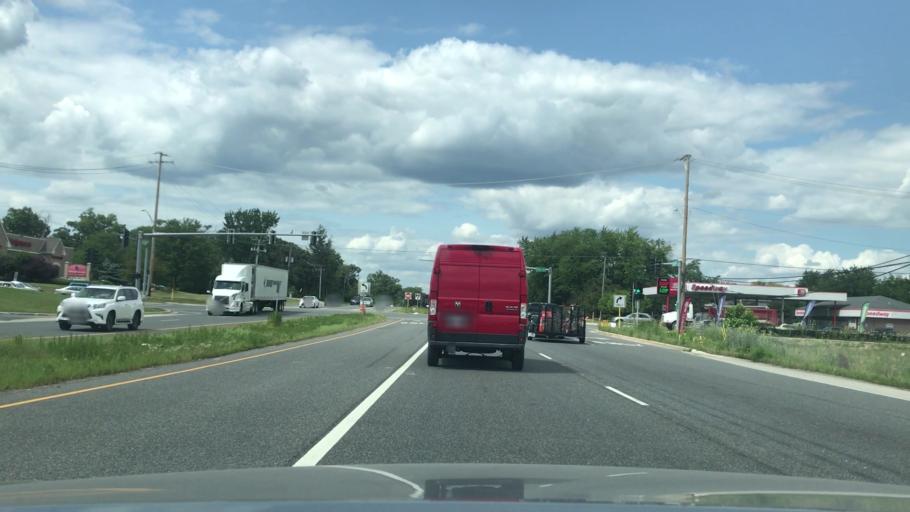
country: US
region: Illinois
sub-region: DuPage County
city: Burr Ridge
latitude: 41.7225
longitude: -87.9436
